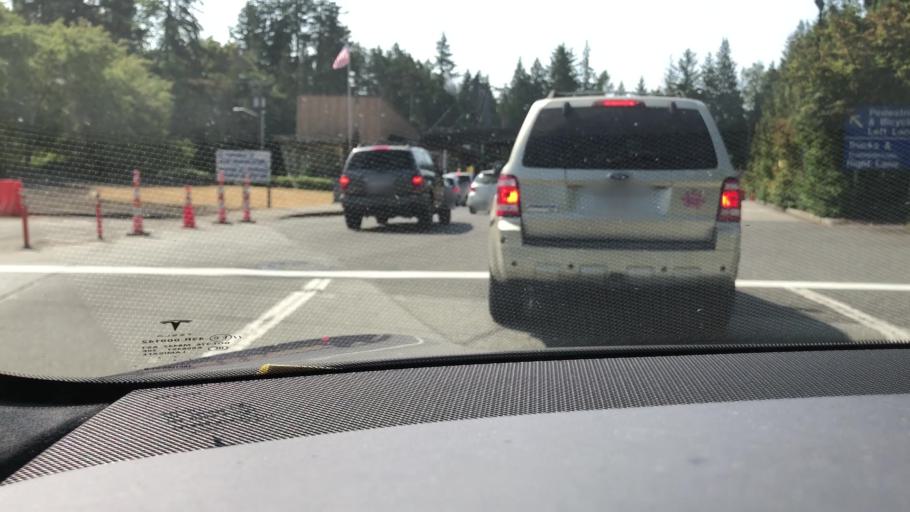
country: US
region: Washington
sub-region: Whatcom County
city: Point Roberts
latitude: 49.0020
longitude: -123.0686
